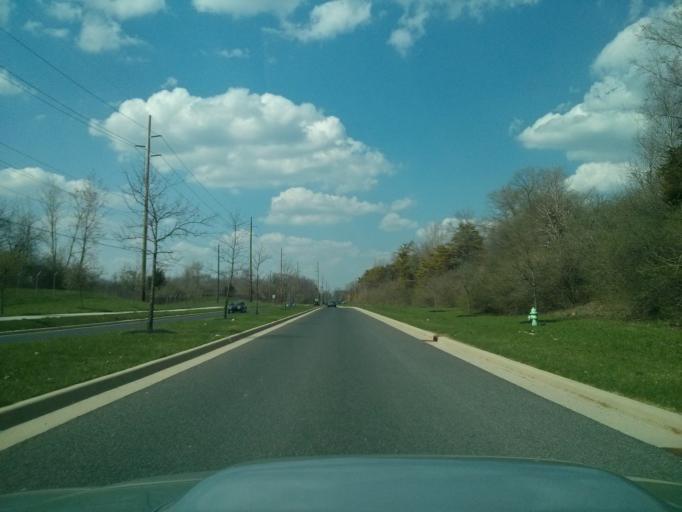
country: US
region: Indiana
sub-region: Hamilton County
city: Carmel
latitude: 39.9375
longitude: -86.0886
